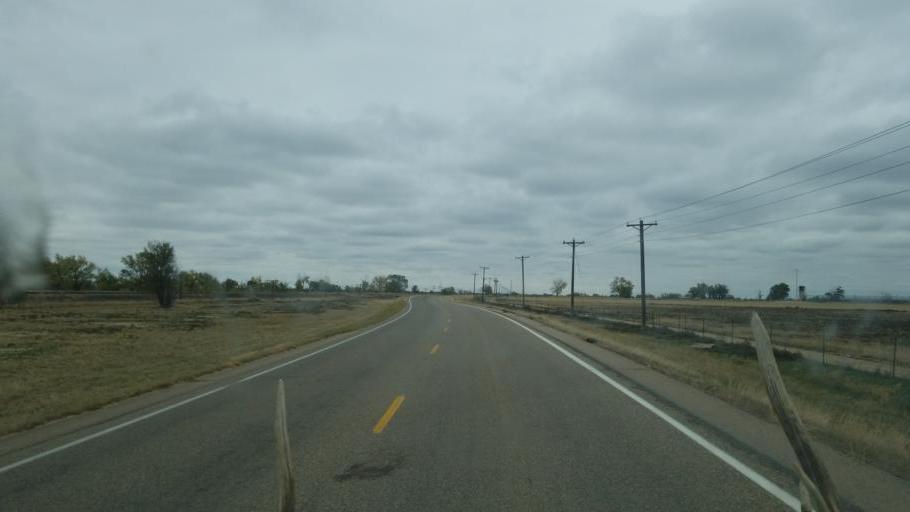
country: US
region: Colorado
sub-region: Crowley County
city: Ordway
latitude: 38.1944
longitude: -103.8481
